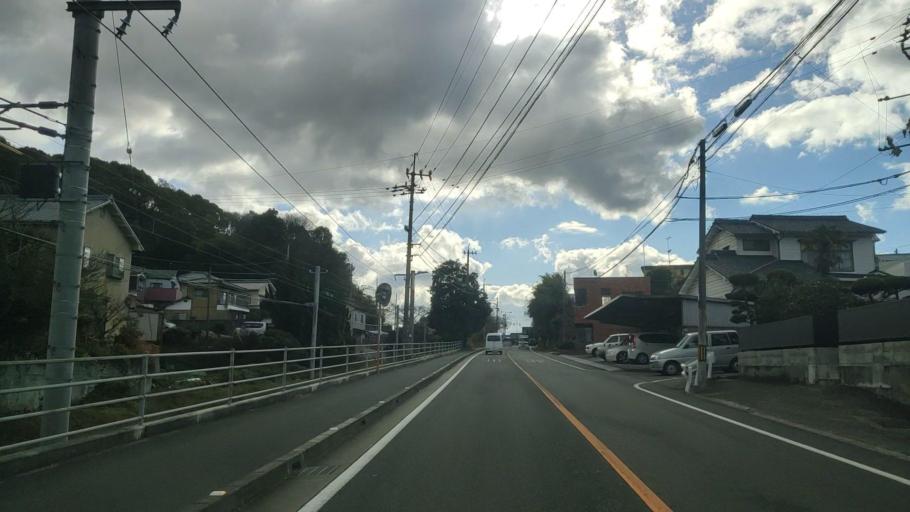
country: JP
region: Ehime
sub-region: Shikoku-chuo Shi
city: Matsuyama
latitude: 33.8795
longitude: 132.7029
